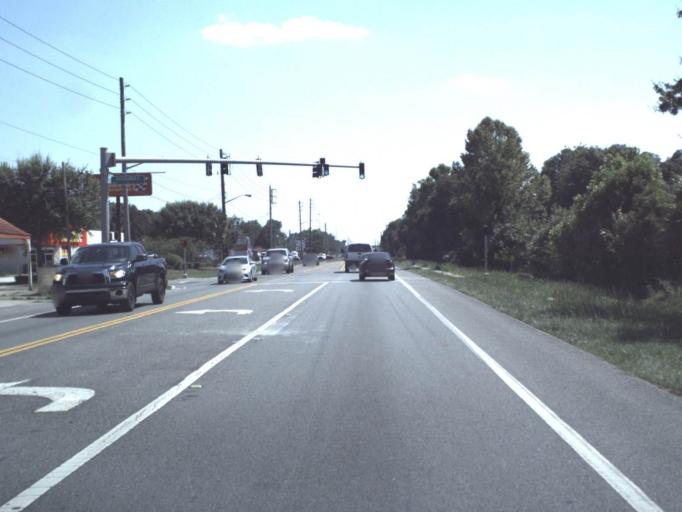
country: US
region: Florida
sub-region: Duval County
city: Jacksonville
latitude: 30.4676
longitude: -81.6326
